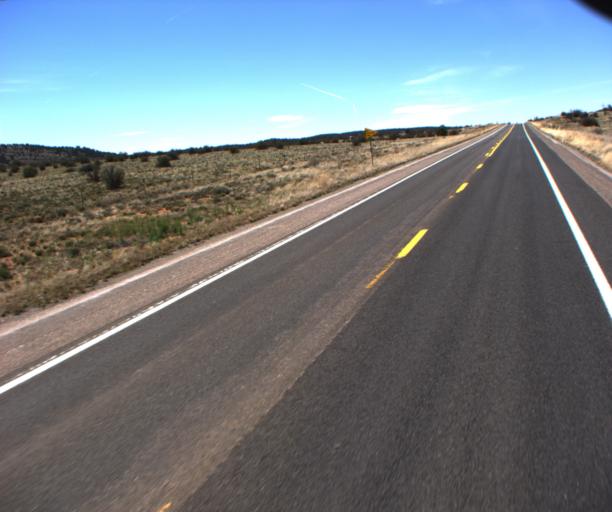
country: US
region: Arizona
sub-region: Mohave County
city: Peach Springs
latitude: 35.4923
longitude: -113.1596
